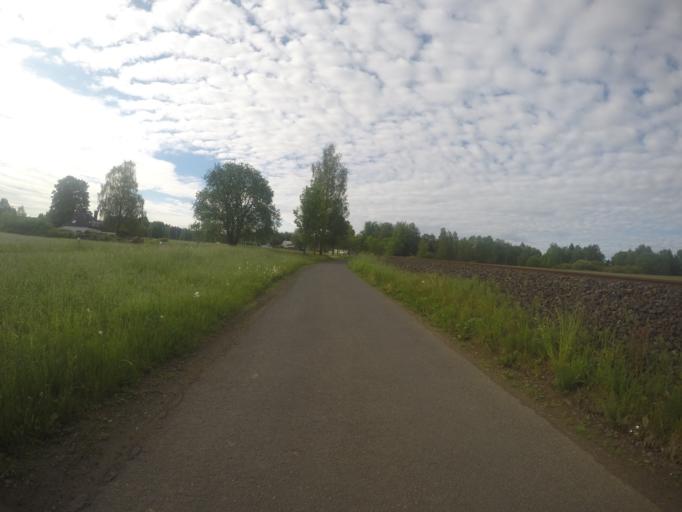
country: DE
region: Bavaria
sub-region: Upper Franconia
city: Schonwald
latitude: 50.2110
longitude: 12.1015
